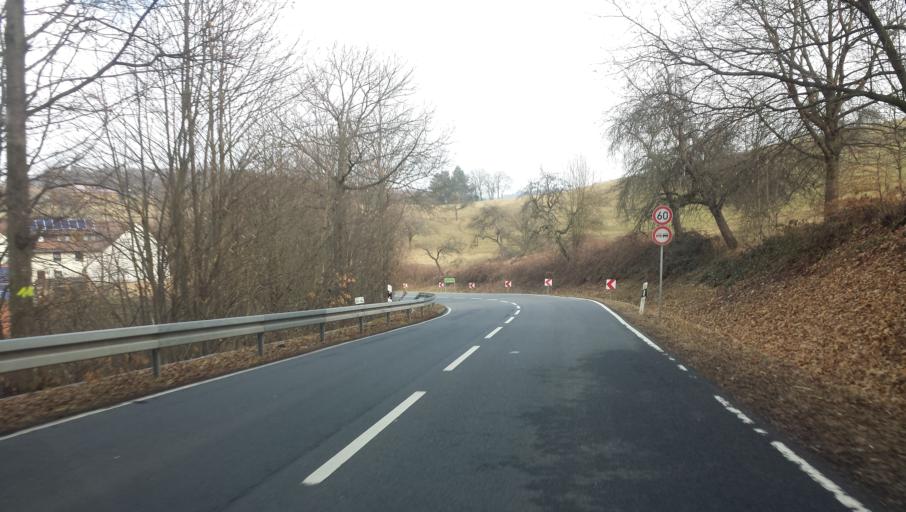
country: DE
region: Hesse
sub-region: Regierungsbezirk Darmstadt
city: Frankisch-Crumbach
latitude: 49.7200
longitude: 8.8880
